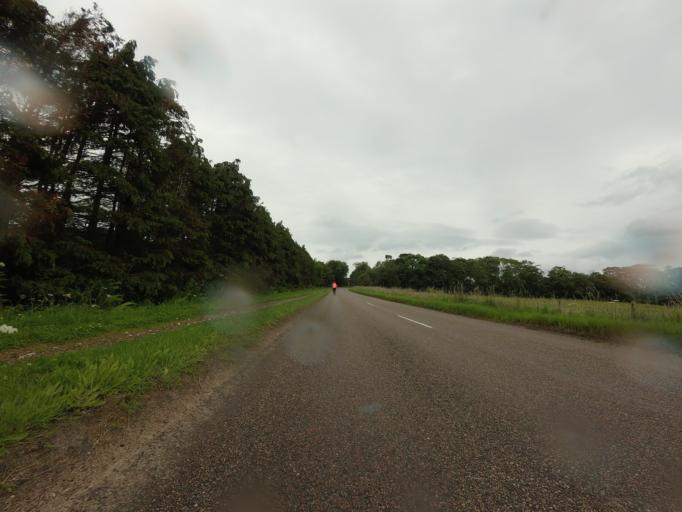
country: GB
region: Scotland
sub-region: Moray
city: Cullen
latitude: 57.6822
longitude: -2.8141
